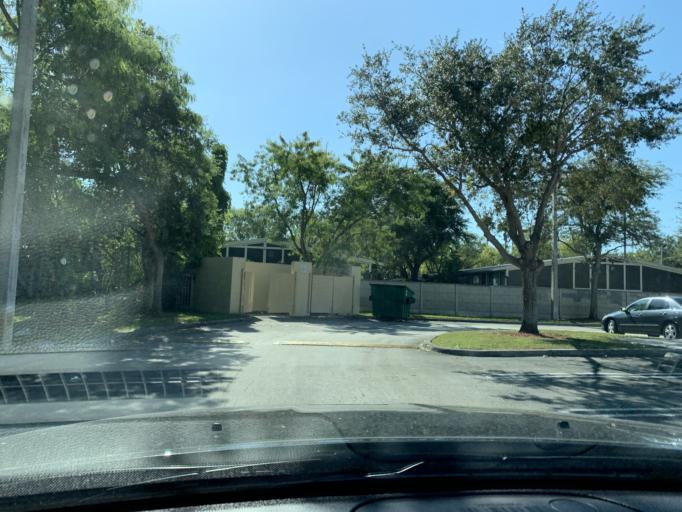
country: US
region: Florida
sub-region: Miami-Dade County
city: Richmond West
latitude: 25.6239
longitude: -80.4128
